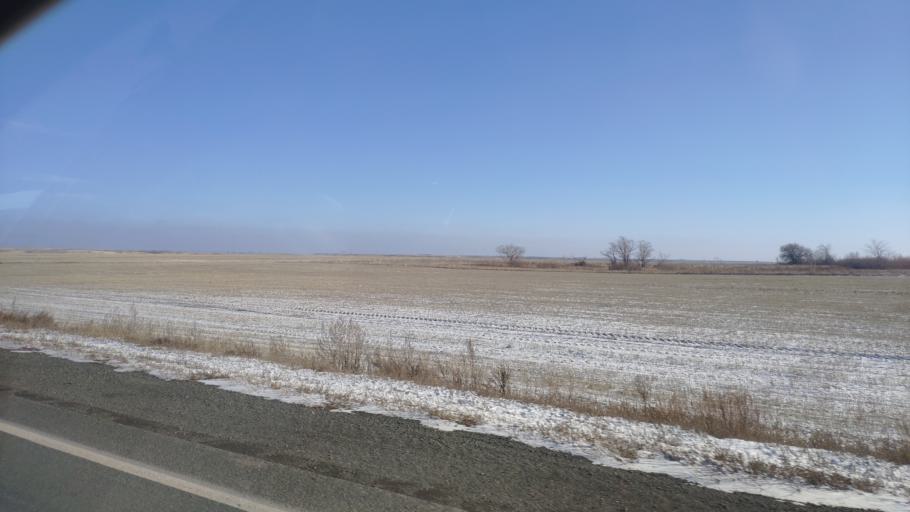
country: RU
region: Orenburg
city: Mednogorsk
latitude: 51.3248
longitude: 57.6081
